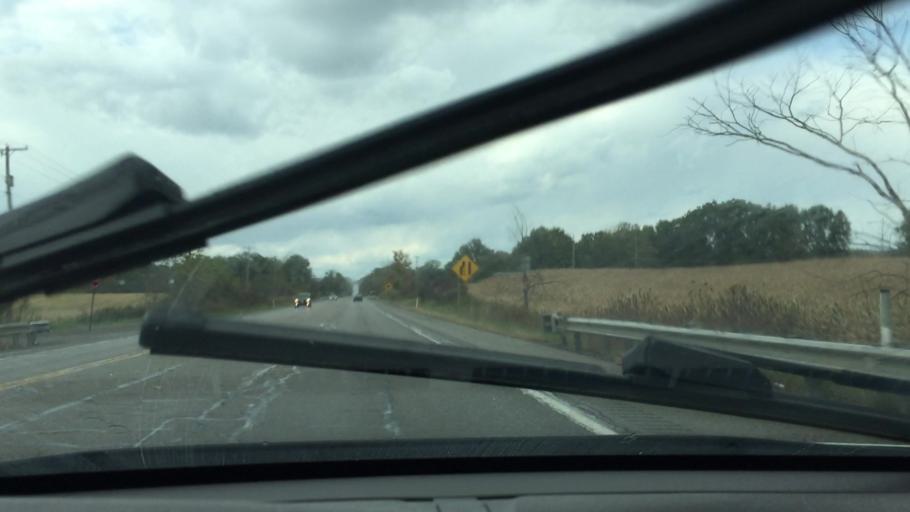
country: US
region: Ohio
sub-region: Mahoning County
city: Lowellville
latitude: 41.0662
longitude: -80.4633
